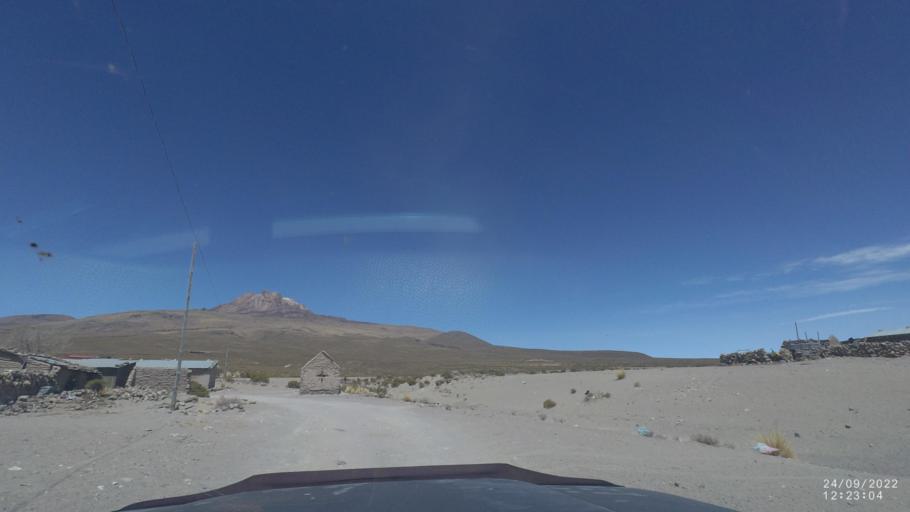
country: BO
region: Potosi
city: Colchani
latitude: -19.7611
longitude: -67.6644
